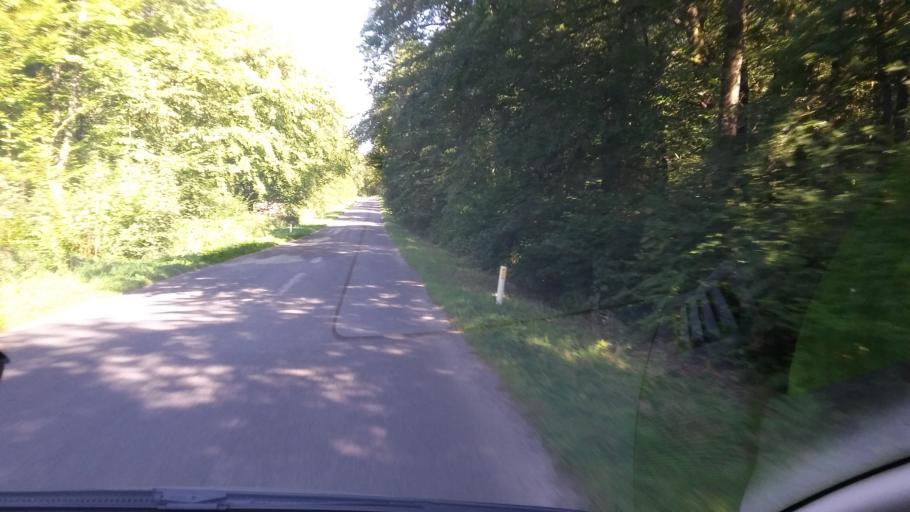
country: BE
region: Wallonia
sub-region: Province du Luxembourg
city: Neufchateau
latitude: 49.7982
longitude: 5.4166
